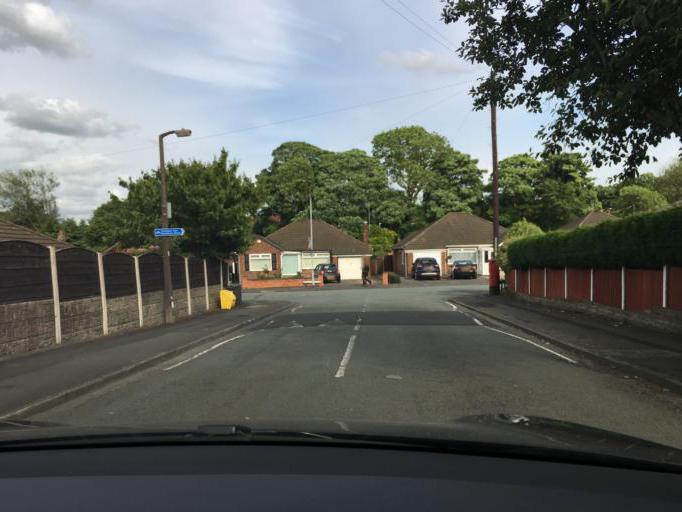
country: GB
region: England
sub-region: Borough of Stockport
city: Hazel Grove
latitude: 53.3798
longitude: -2.1145
